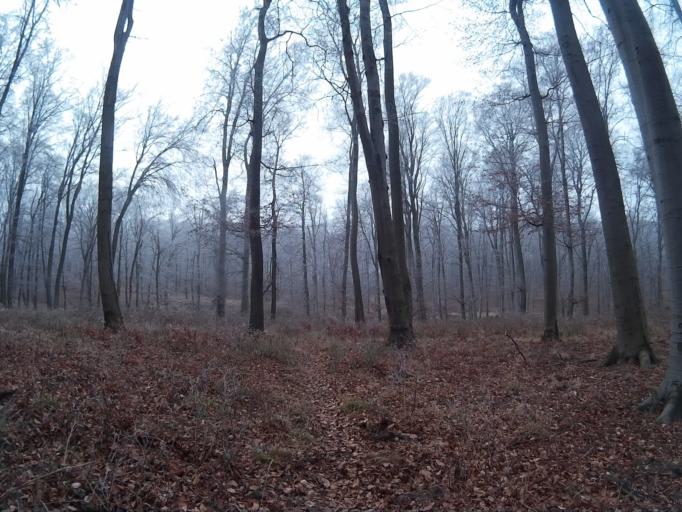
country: HU
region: Komarom-Esztergom
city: Oroszlany
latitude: 47.4283
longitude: 18.3424
